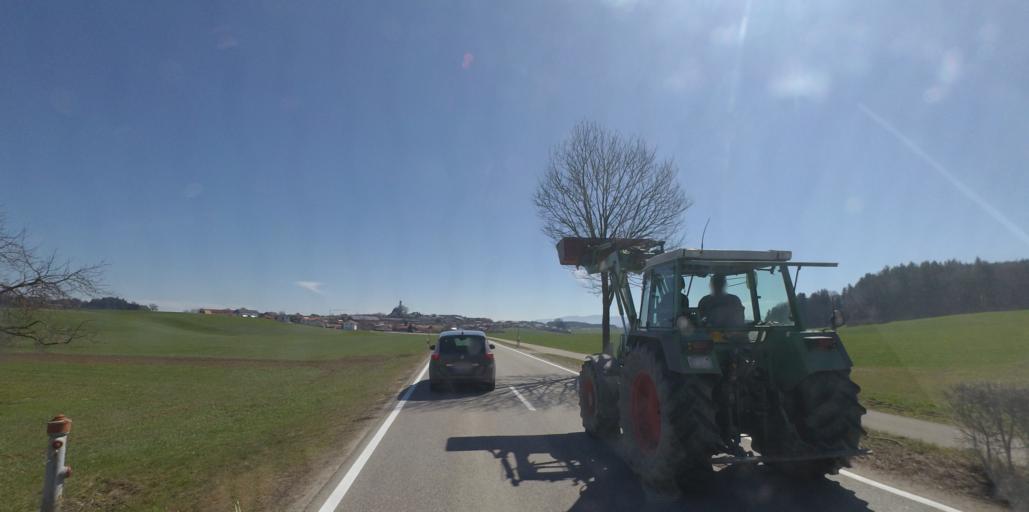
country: DE
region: Bavaria
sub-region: Upper Bavaria
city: Nussdorf
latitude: 47.9090
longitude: 12.5829
